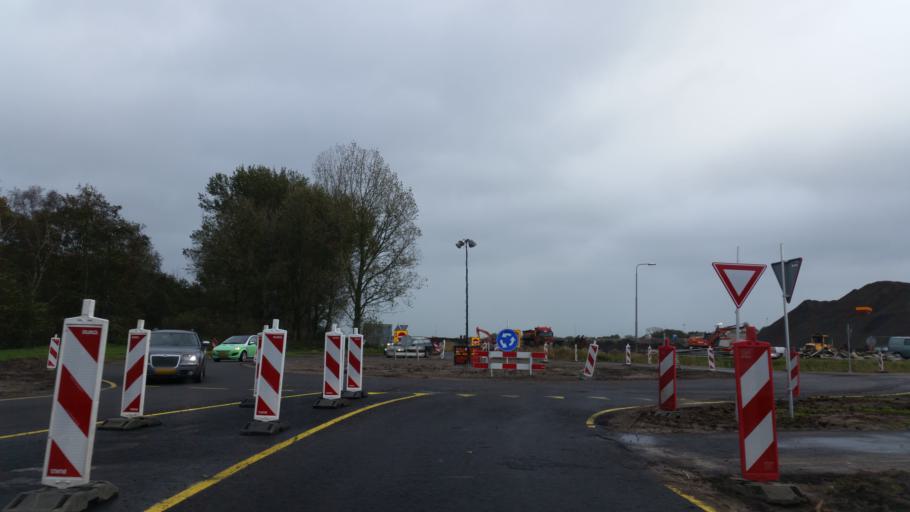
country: NL
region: Friesland
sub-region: Gemeente Skarsterlan
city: Joure
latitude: 52.9598
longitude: 5.8148
